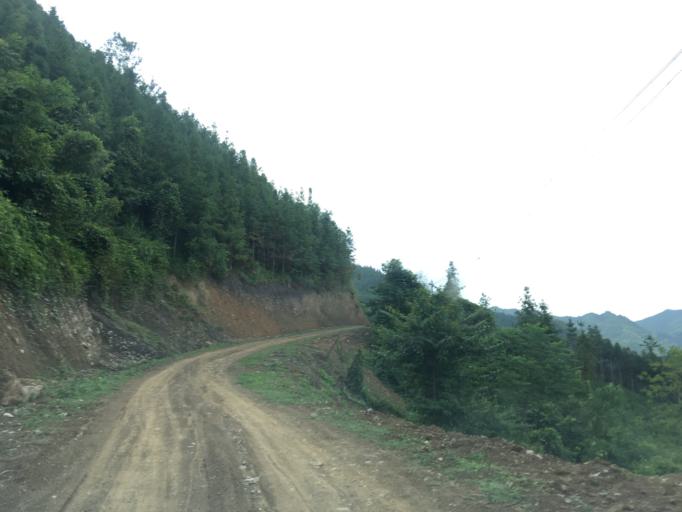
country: CN
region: Guangxi Zhuangzu Zizhiqu
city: Xinzhou
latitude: 24.8705
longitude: 105.8461
